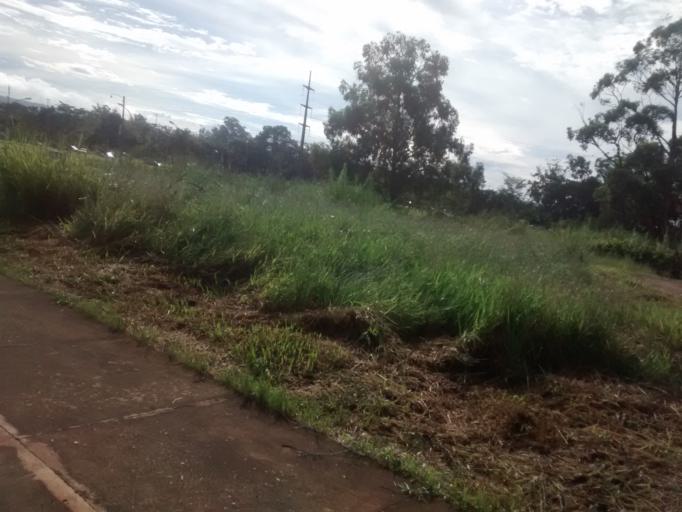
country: BR
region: Federal District
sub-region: Brasilia
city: Brasilia
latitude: -15.7681
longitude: -47.8648
